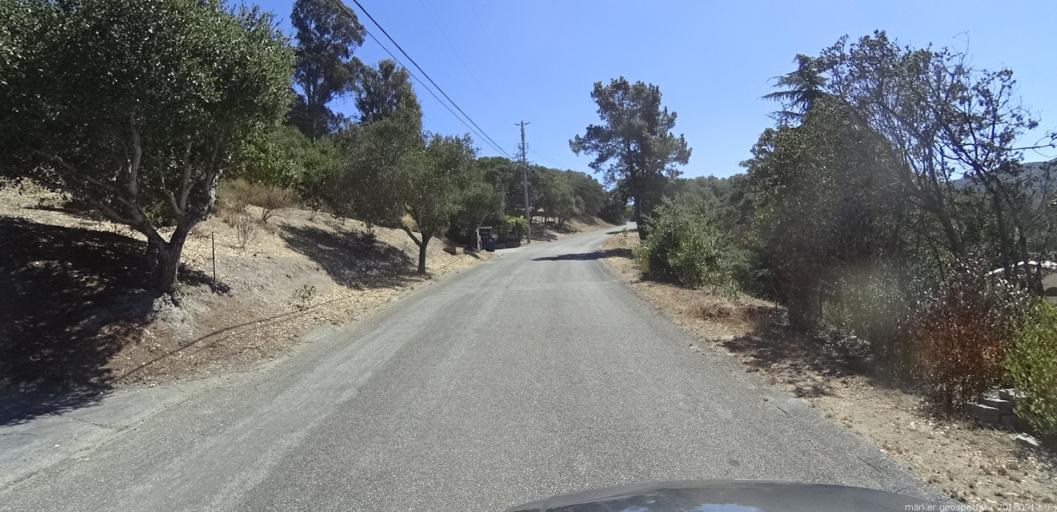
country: US
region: California
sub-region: Monterey County
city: Carmel Valley Village
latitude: 36.4889
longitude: -121.7373
